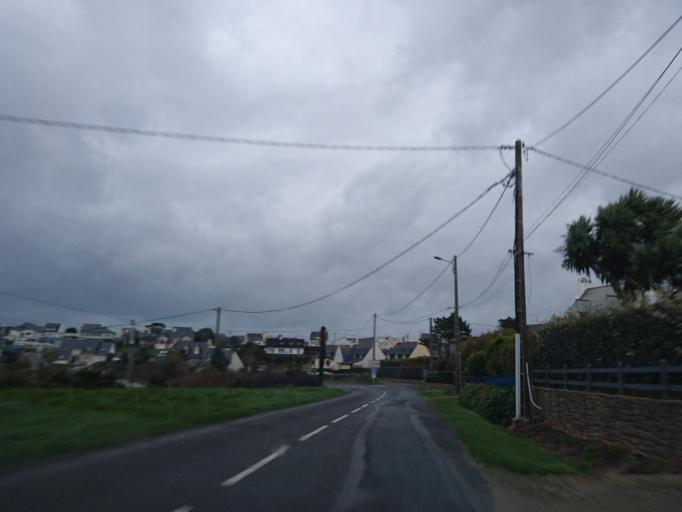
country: FR
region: Brittany
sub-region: Departement du Finistere
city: Le Conquet
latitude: 48.3514
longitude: -4.7732
